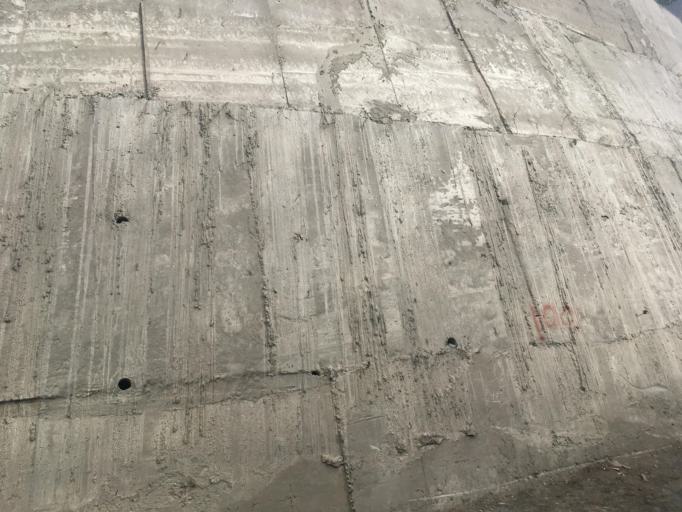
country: PK
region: Gilgit-Baltistan
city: Skardu
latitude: 35.2962
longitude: 75.6475
